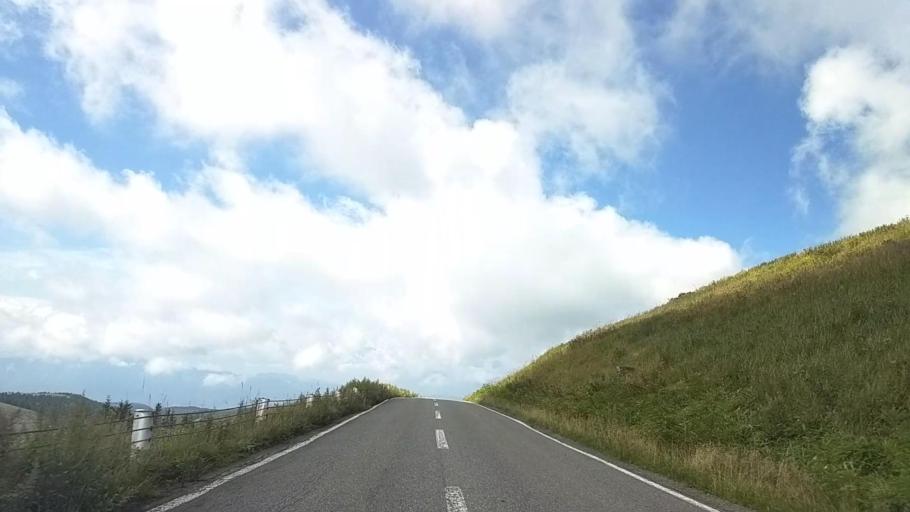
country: JP
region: Nagano
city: Suwa
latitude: 36.0981
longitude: 138.1810
